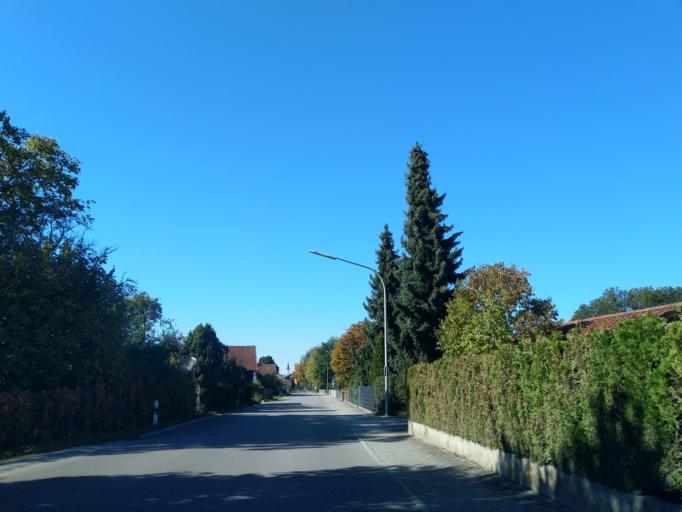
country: DE
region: Bavaria
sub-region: Lower Bavaria
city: Stephansposching
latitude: 48.8187
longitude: 12.8192
